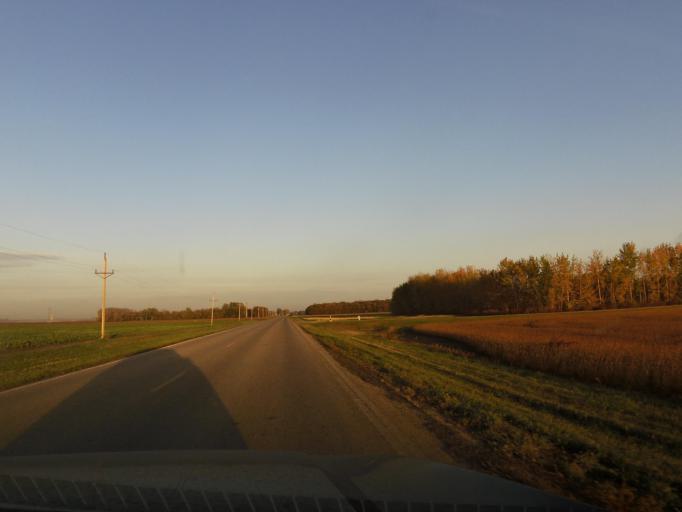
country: CA
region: Manitoba
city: Altona
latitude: 48.9634
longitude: -97.2870
